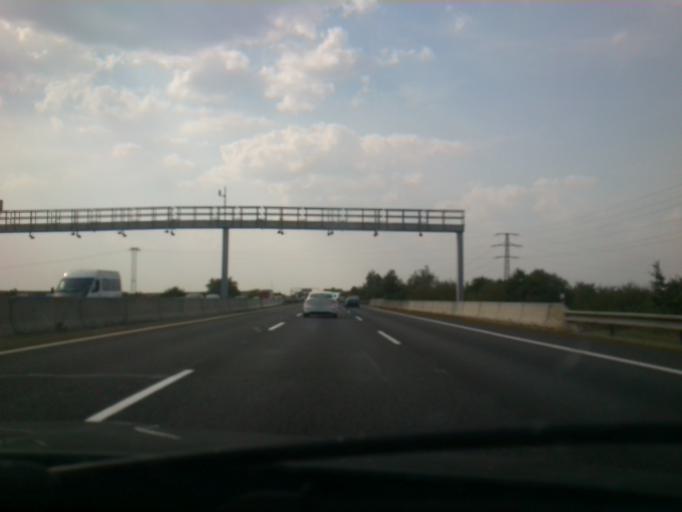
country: CZ
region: Central Bohemia
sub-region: Okres Praha-Vychod
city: Strancice
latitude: 49.9408
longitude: 14.6705
